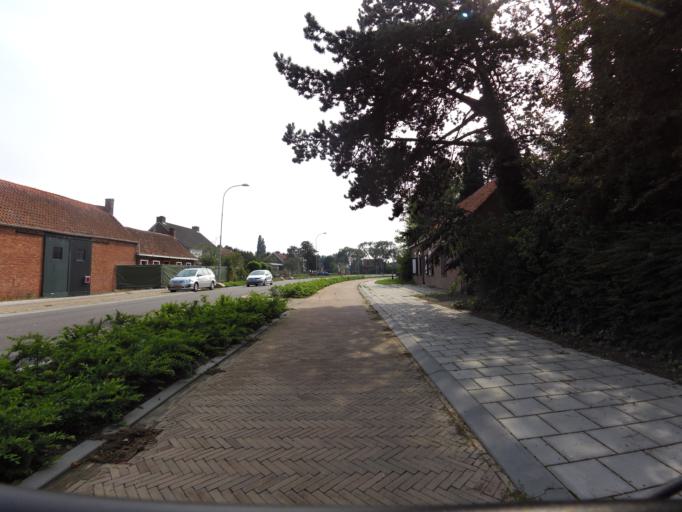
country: NL
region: Zeeland
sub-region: Gemeente Middelburg
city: Middelburg
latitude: 51.5235
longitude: 3.6057
